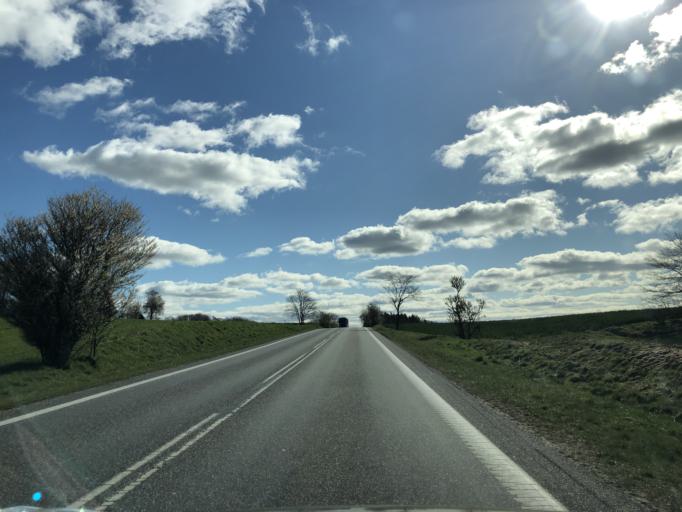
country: DK
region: North Denmark
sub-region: Mariagerfjord Kommune
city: Hobro
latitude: 56.6140
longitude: 9.6341
